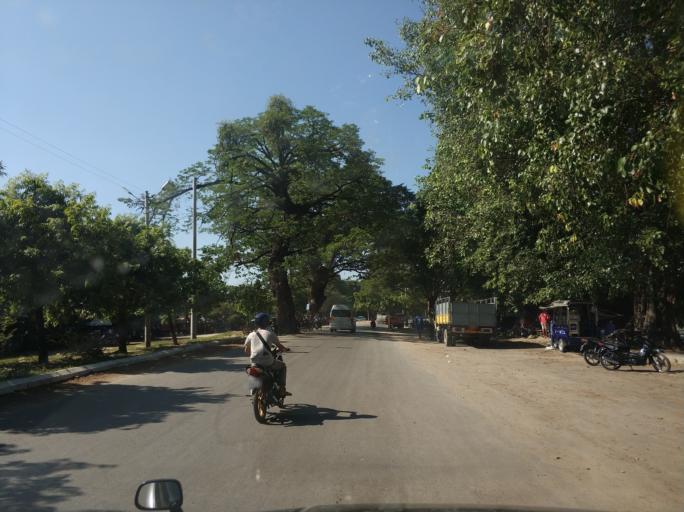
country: MM
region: Mandalay
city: Mandalay
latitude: 21.9691
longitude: 96.0563
